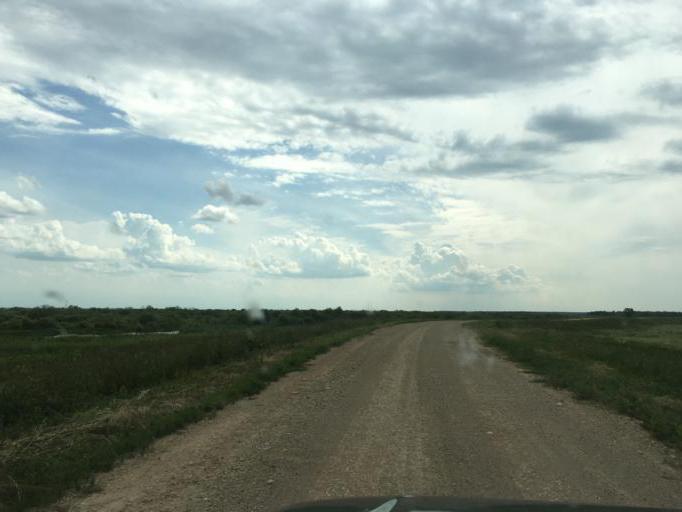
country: LV
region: Lubana
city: Lubana
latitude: 56.8060
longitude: 26.8469
